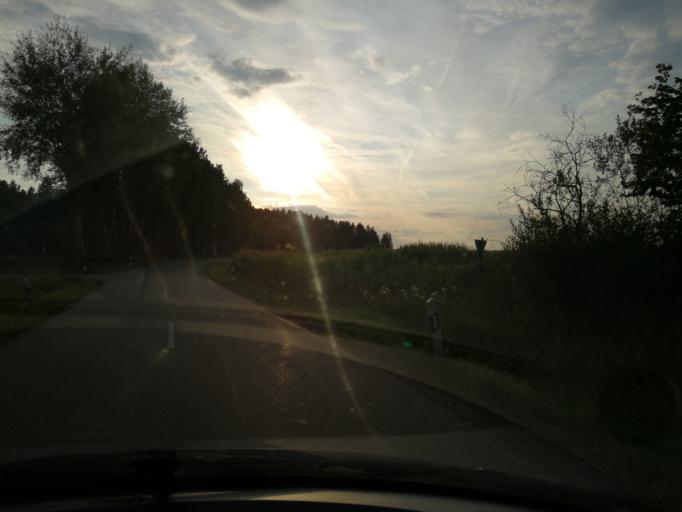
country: DE
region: Bavaria
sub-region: Lower Bavaria
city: Wiesenfelden
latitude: 49.0490
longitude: 12.5281
